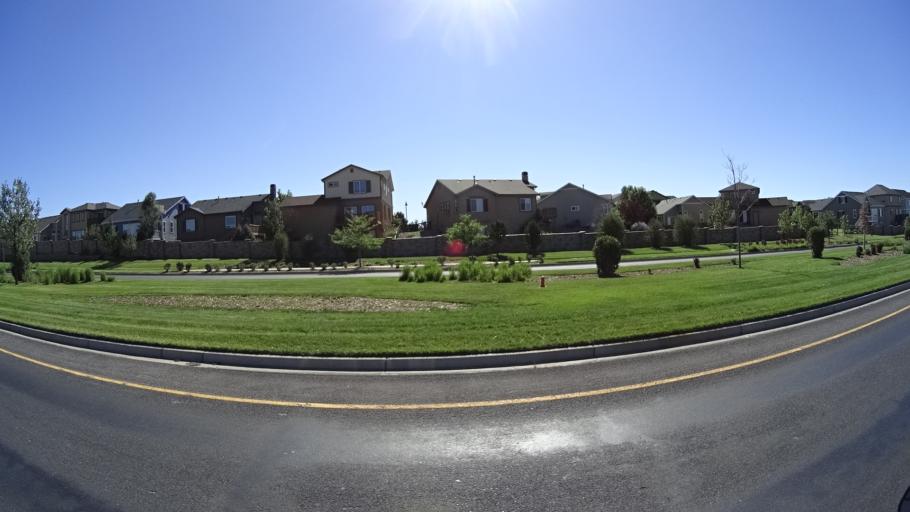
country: US
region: Colorado
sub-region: El Paso County
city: Cimarron Hills
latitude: 38.9320
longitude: -104.6830
